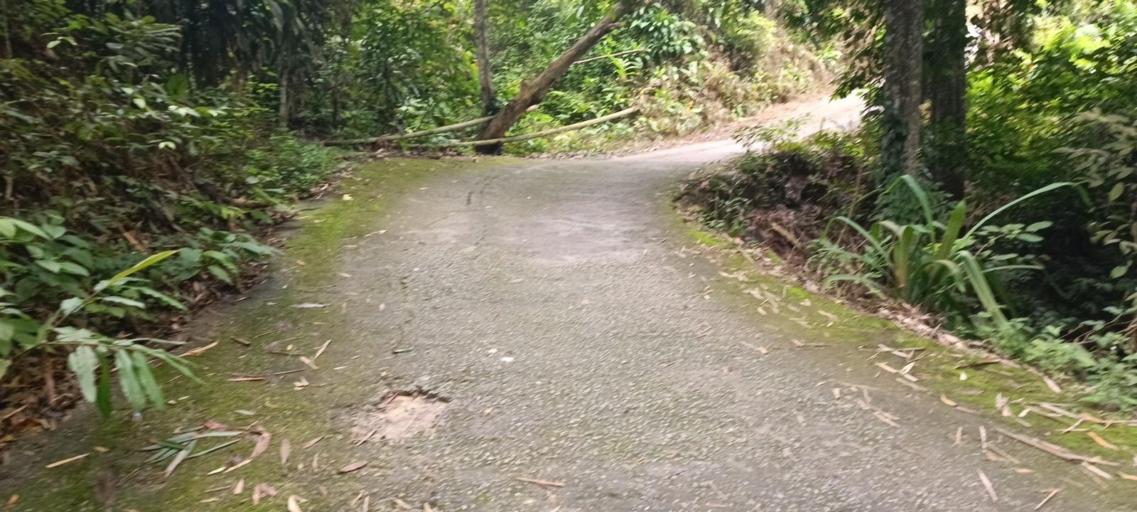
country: MY
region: Penang
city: Tanjung Tokong
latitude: 5.4052
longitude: 100.2631
